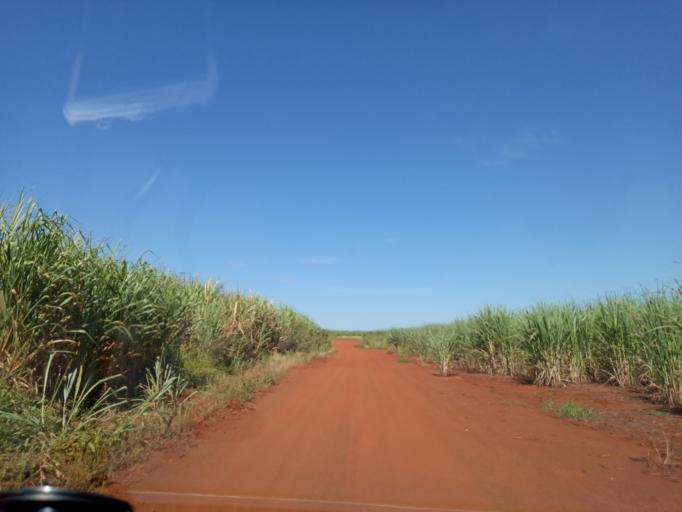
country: BR
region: Goias
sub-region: Itumbiara
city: Itumbiara
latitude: -18.4551
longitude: -49.1484
